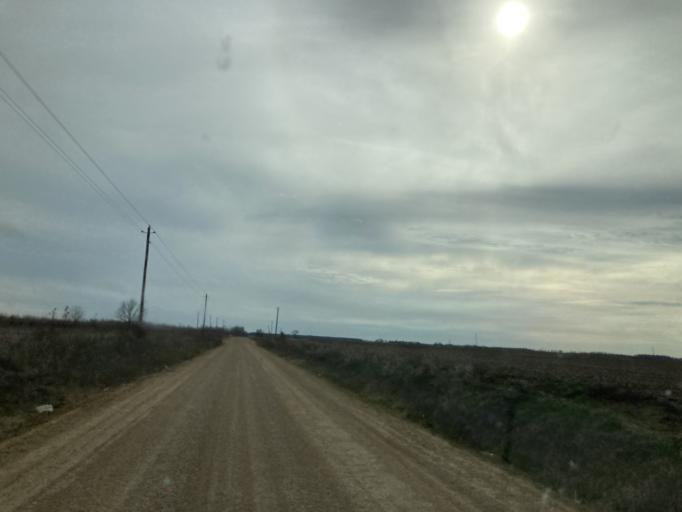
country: US
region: Mississippi
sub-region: Humphreys County
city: Belzoni
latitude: 33.1706
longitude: -90.5723
